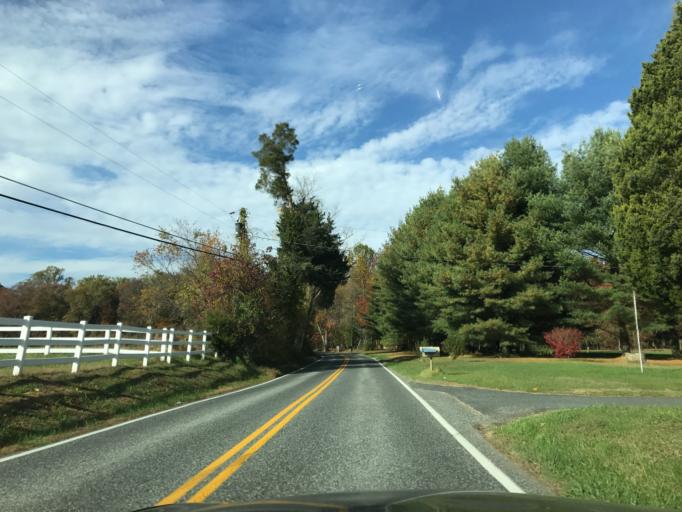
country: US
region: Maryland
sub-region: Harford County
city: Joppatowne
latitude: 39.4573
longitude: -76.3756
